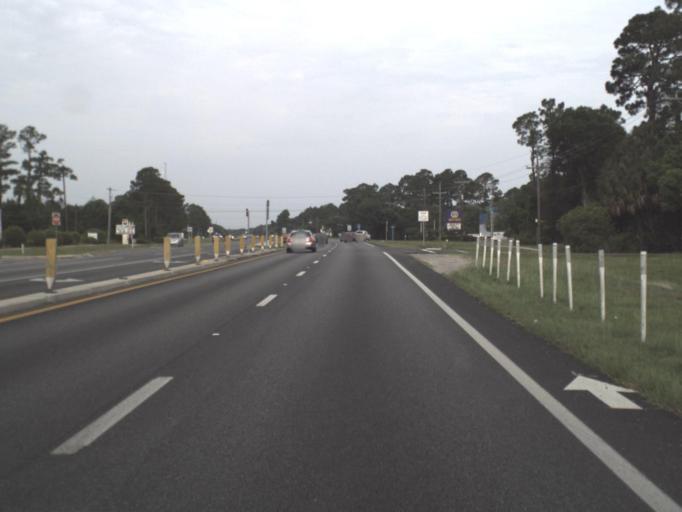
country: US
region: Florida
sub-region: Saint Johns County
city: Saint Augustine
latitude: 29.9164
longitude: -81.3468
